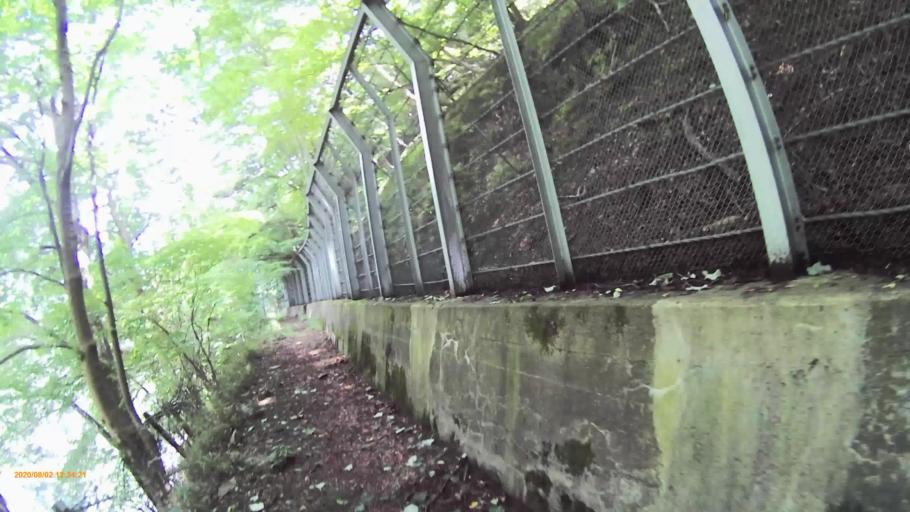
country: JP
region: Nagano
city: Shiojiri
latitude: 36.0361
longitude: 137.8824
